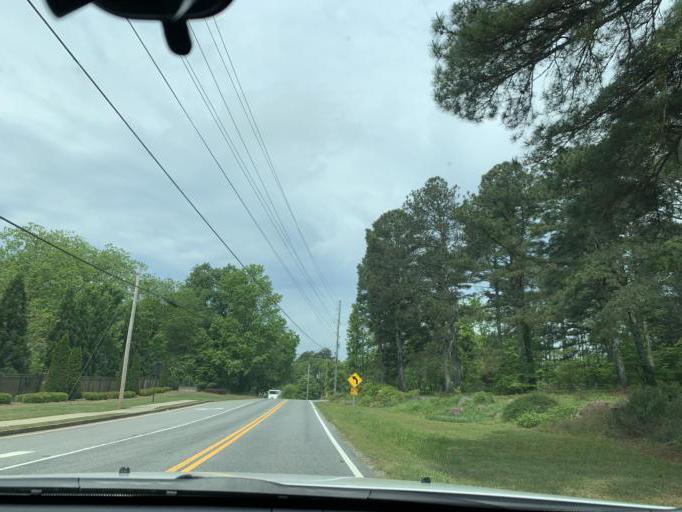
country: US
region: Georgia
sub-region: Forsyth County
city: Cumming
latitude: 34.1359
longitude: -84.1837
